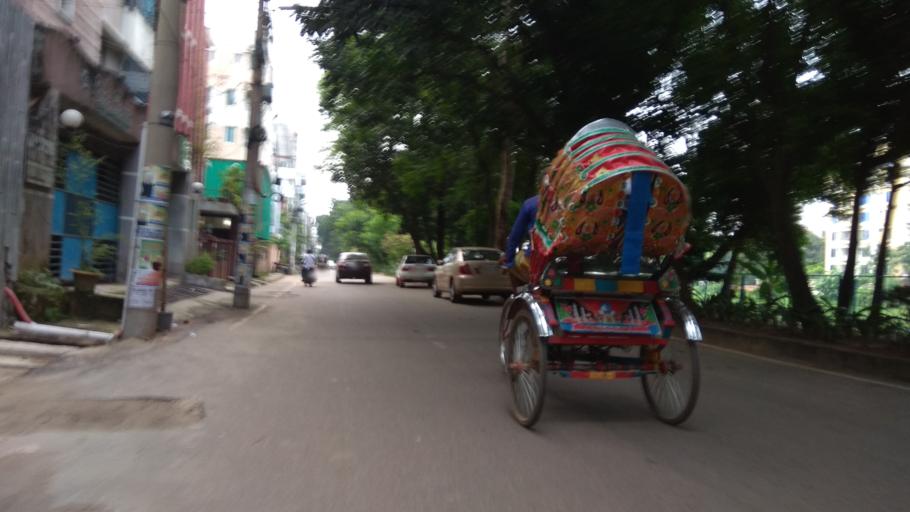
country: BD
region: Dhaka
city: Tungi
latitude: 23.8659
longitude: 90.3923
